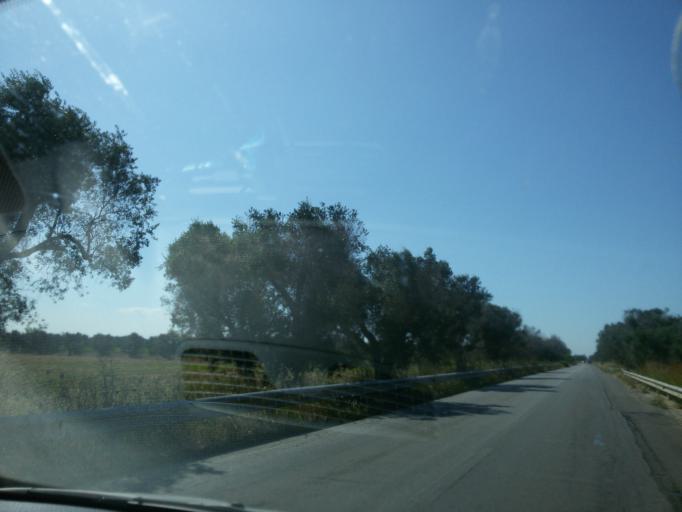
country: IT
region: Apulia
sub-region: Provincia di Brindisi
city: San Donaci
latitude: 40.4612
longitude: 17.9093
